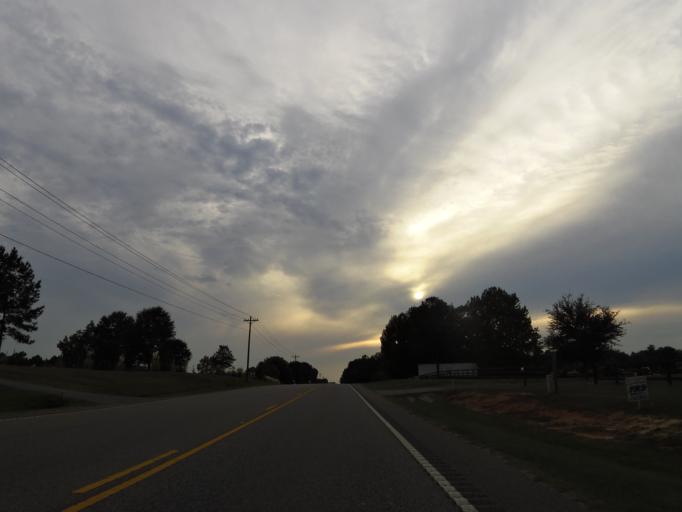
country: US
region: Alabama
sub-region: Escambia County
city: Atmore
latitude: 31.0045
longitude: -87.5834
